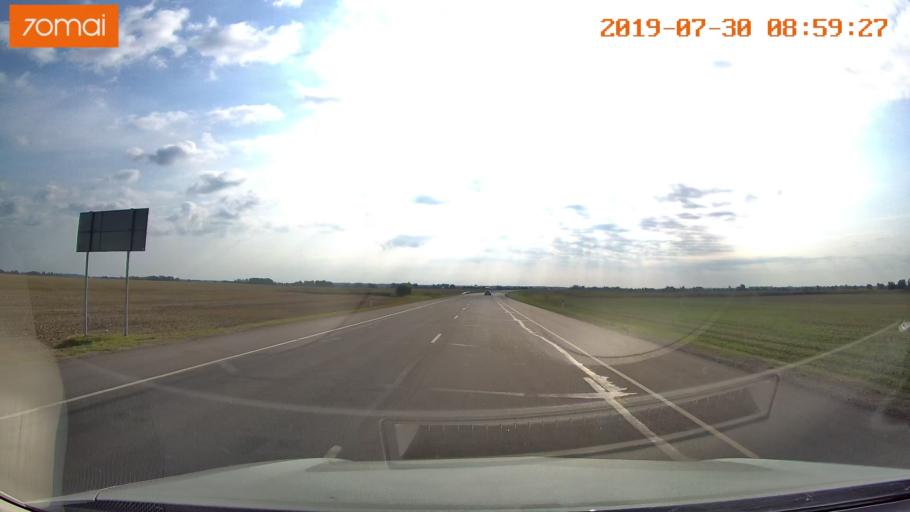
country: RU
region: Kaliningrad
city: Gusev
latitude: 54.6144
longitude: 22.1548
